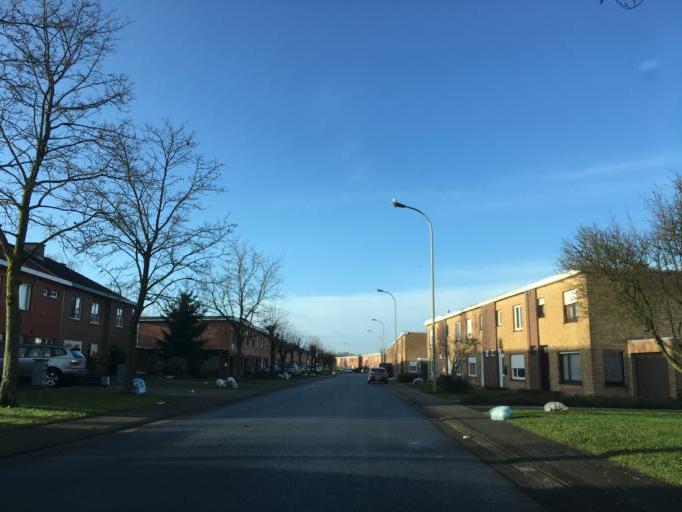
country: BE
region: Flanders
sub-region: Provincie West-Vlaanderen
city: Roeselare
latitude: 50.9622
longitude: 3.1126
